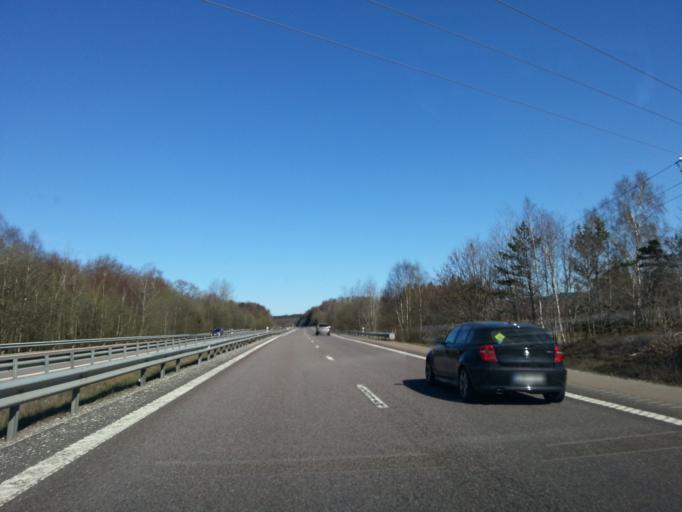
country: SE
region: Vaestra Goetaland
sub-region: Kungalvs Kommun
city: Kode
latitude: 57.9250
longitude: 11.8778
